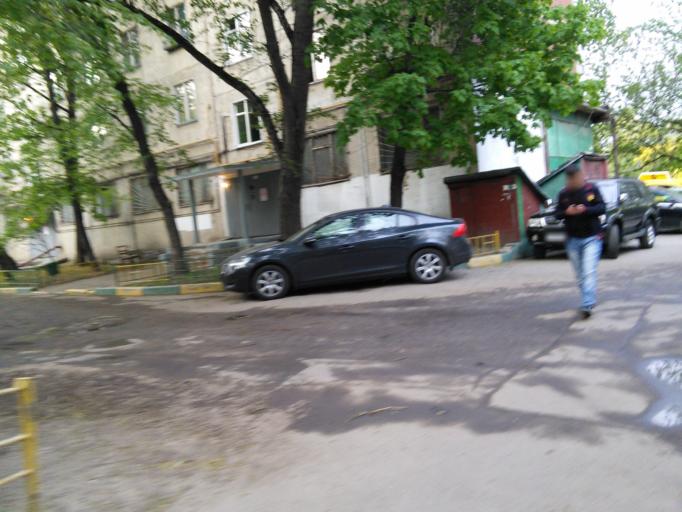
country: RU
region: Moscow
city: Mar'ina Roshcha
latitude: 55.8045
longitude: 37.6141
